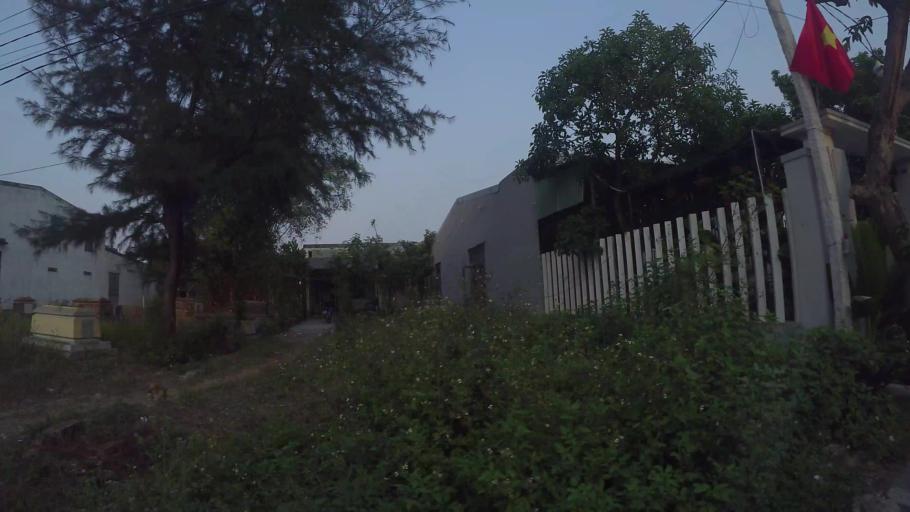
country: VN
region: Da Nang
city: Ngu Hanh Son
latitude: 15.9528
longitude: 108.2531
